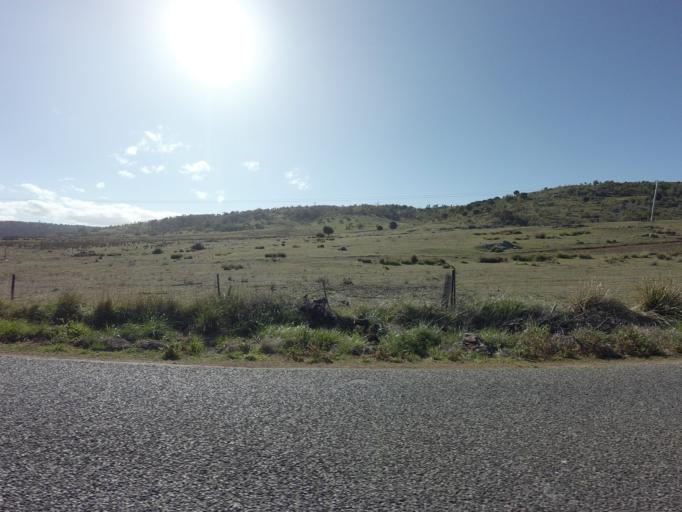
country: AU
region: Tasmania
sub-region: Sorell
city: Sorell
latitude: -42.1947
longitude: 148.0558
